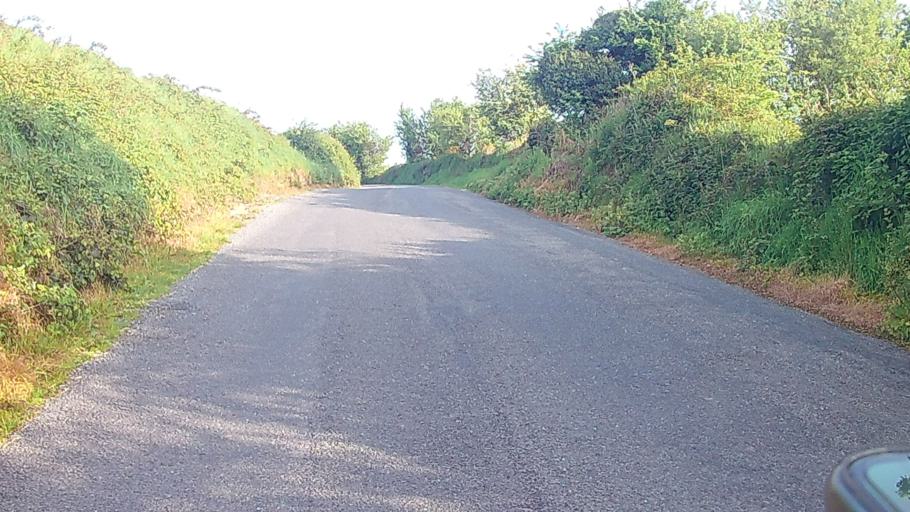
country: IE
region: Munster
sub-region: County Cork
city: Cork
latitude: 51.9757
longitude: -8.4636
